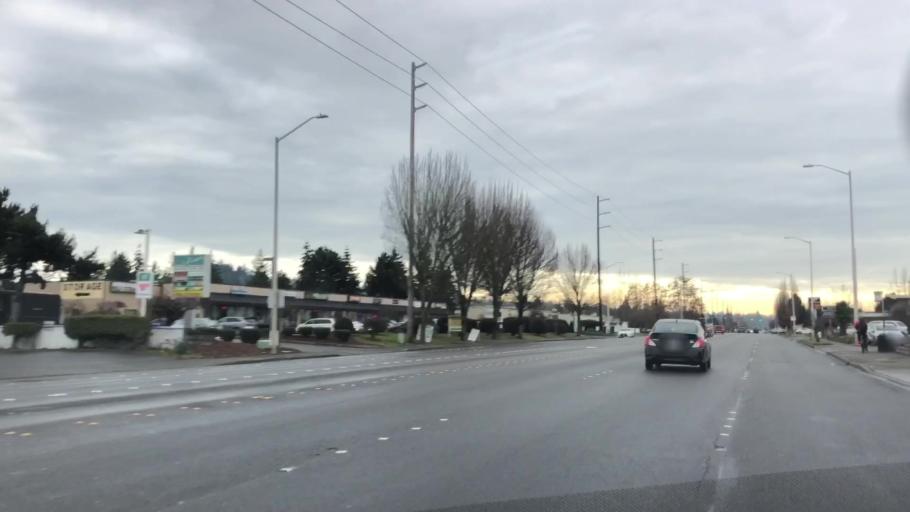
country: US
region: Washington
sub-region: King County
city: Kent
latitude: 47.4117
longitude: -122.2281
